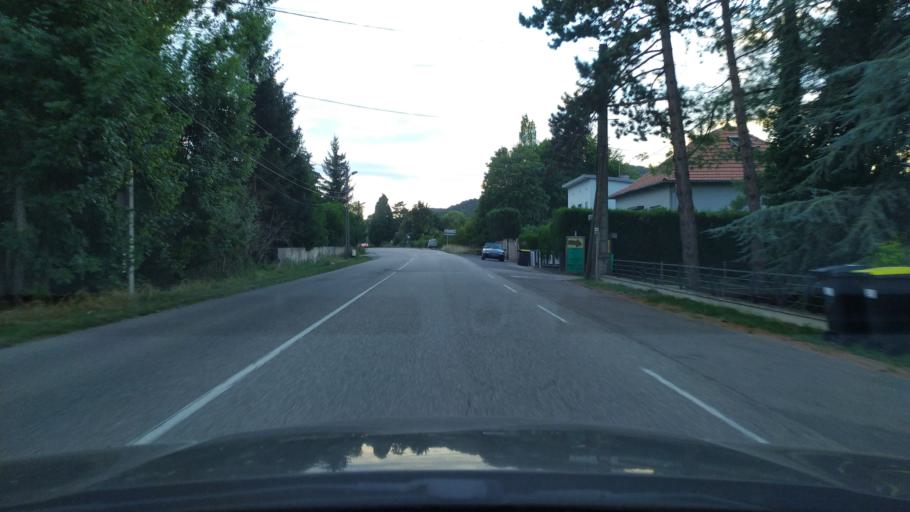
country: FR
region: Lorraine
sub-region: Departement de la Moselle
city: Moulins-les-Metz
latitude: 49.0950
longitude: 6.0971
